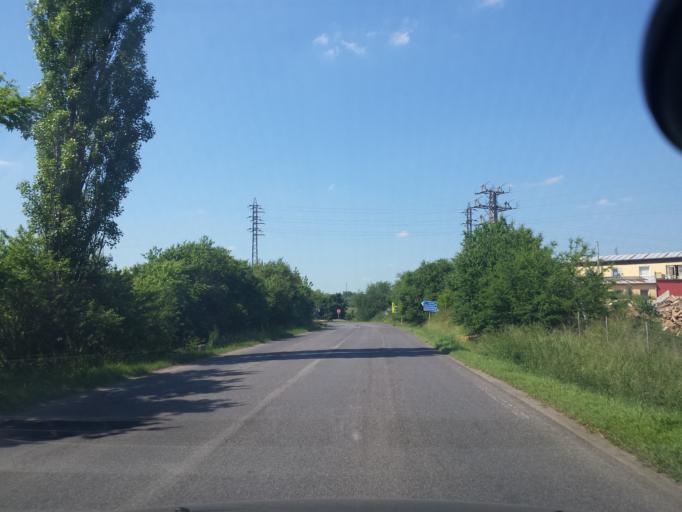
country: CZ
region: Central Bohemia
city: Horomerice
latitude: 50.1438
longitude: 14.3348
